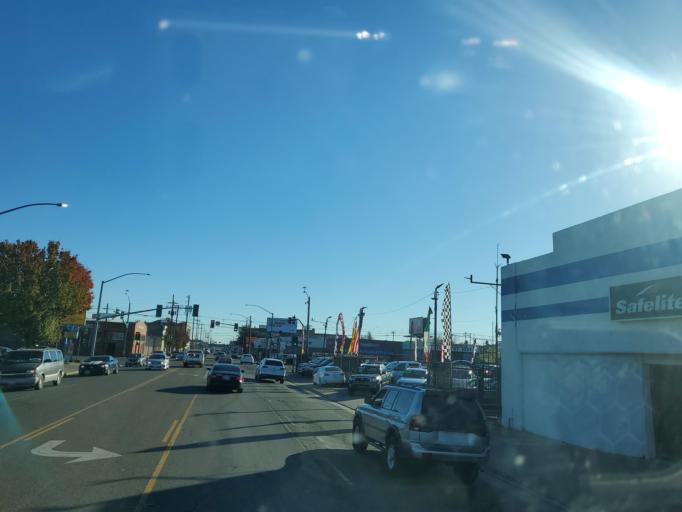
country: US
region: California
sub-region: San Joaquin County
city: Stockton
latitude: 37.9595
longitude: -121.2726
